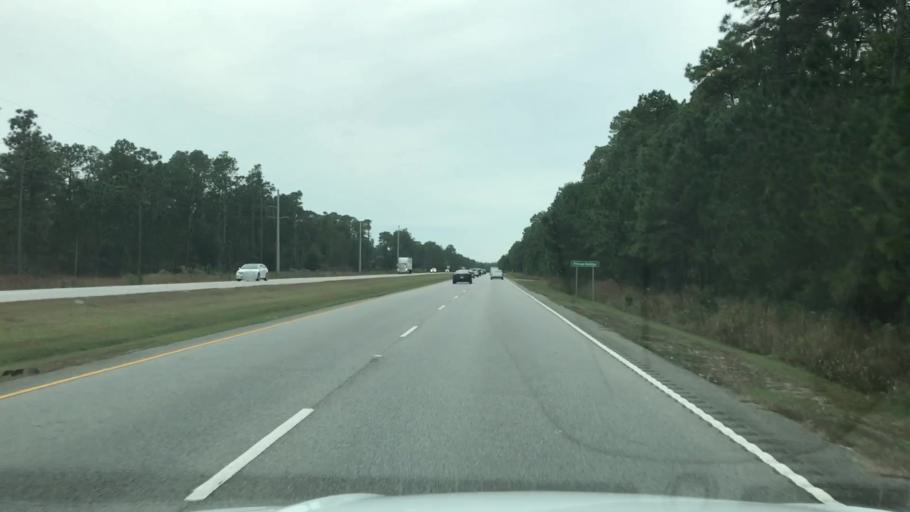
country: US
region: South Carolina
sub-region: Georgetown County
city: Georgetown
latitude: 33.4155
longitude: -79.1844
